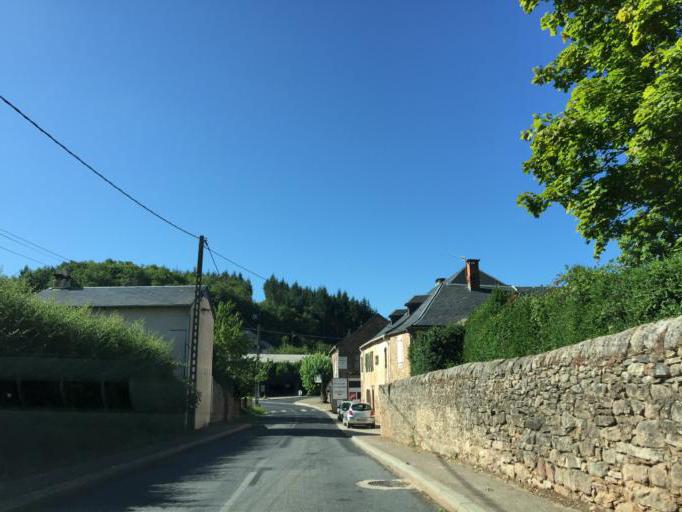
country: FR
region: Midi-Pyrenees
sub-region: Departement de l'Aveyron
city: Saint-Georges-de-Luzencon
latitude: 44.1014
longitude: 2.8990
